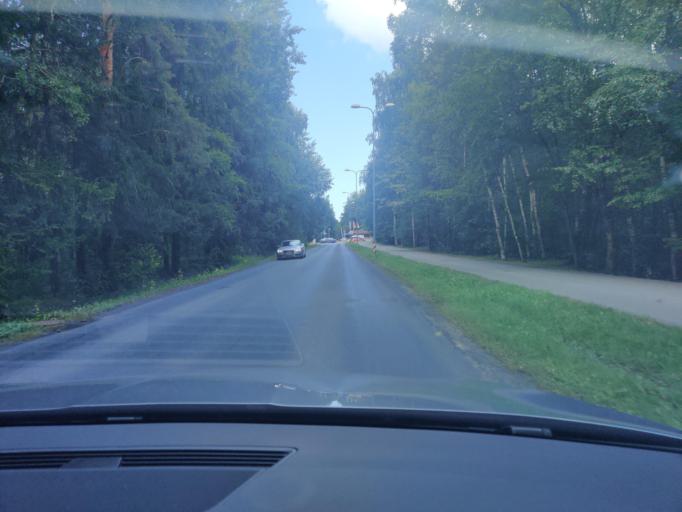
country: EE
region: Harju
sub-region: Saue vald
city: Laagri
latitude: 59.4300
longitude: 24.6360
